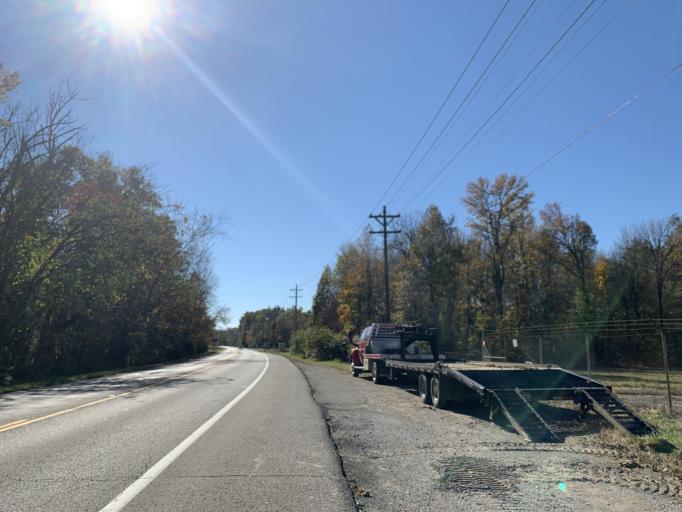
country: US
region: Kentucky
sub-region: Jefferson County
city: Saint Dennis
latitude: 38.1956
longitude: -85.8648
